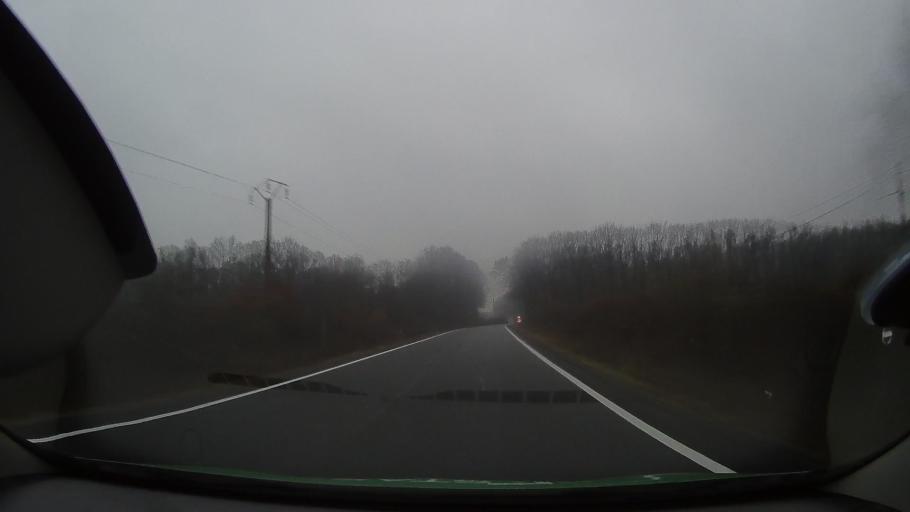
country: RO
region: Bihor
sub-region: Comuna Olcea
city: Olcea
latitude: 46.7039
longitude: 21.9634
